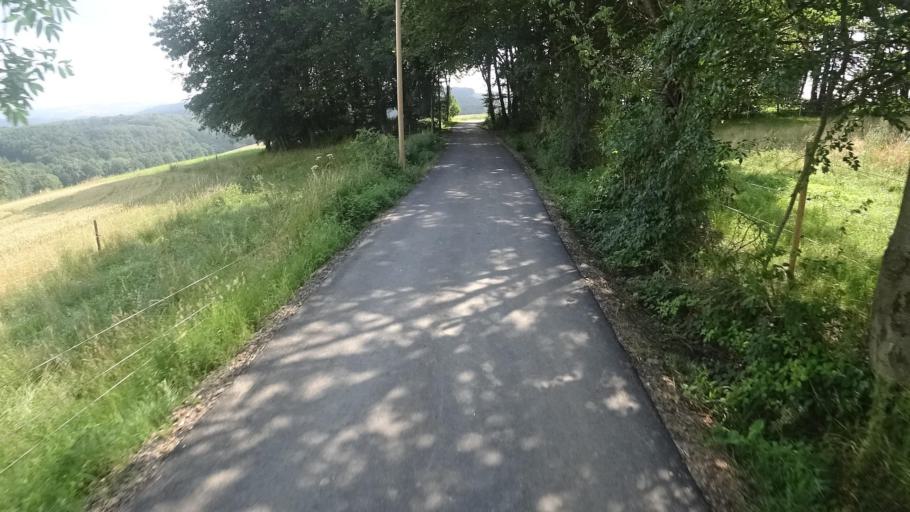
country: DE
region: Rheinland-Pfalz
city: Vettelschoss
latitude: 50.6030
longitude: 7.3427
